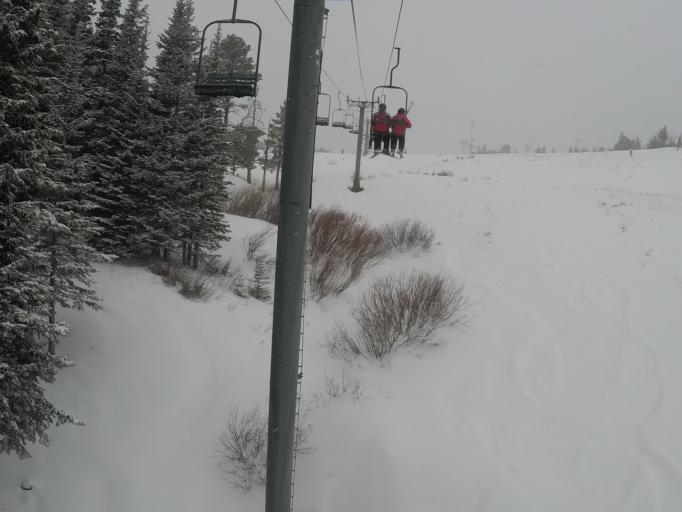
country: US
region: Montana
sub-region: Carbon County
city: Red Lodge
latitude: 45.1920
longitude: -109.3385
